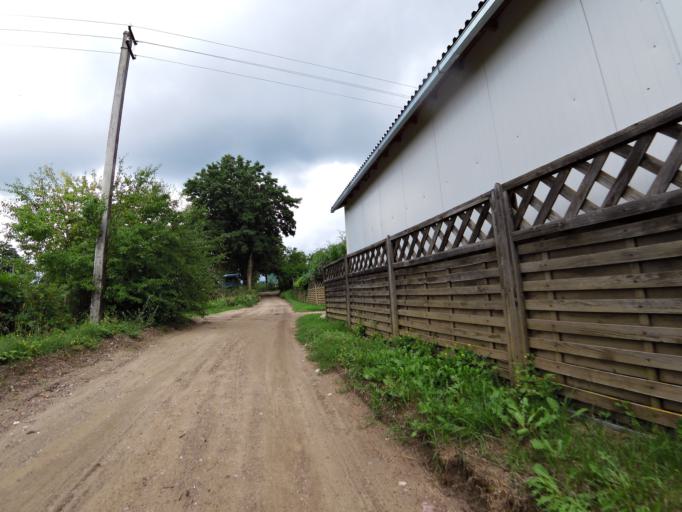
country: LT
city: Grigiskes
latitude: 54.7030
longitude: 25.1093
